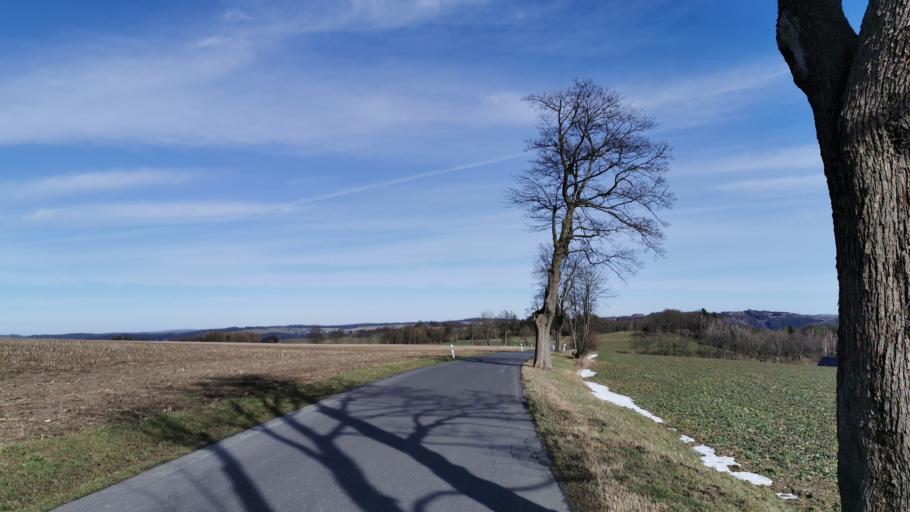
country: DE
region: Bavaria
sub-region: Upper Franconia
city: Ludwigsstadt
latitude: 50.4852
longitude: 11.4518
